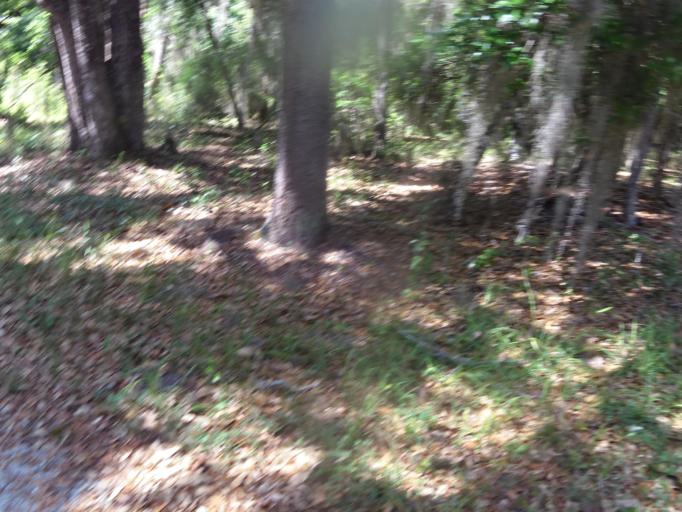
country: US
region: Florida
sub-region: Saint Johns County
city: Palm Valley
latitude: 30.1293
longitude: -81.3668
